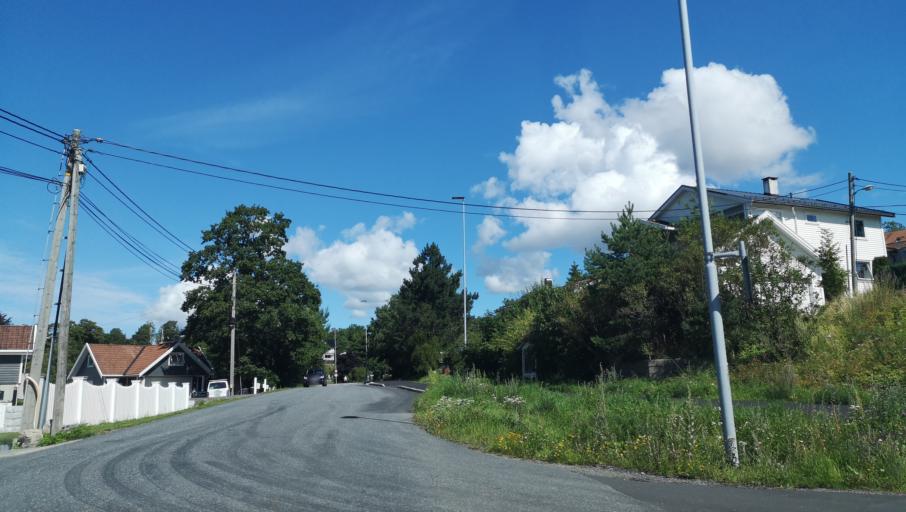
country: NO
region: Akershus
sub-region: Frogn
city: Drobak
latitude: 59.6556
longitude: 10.6414
